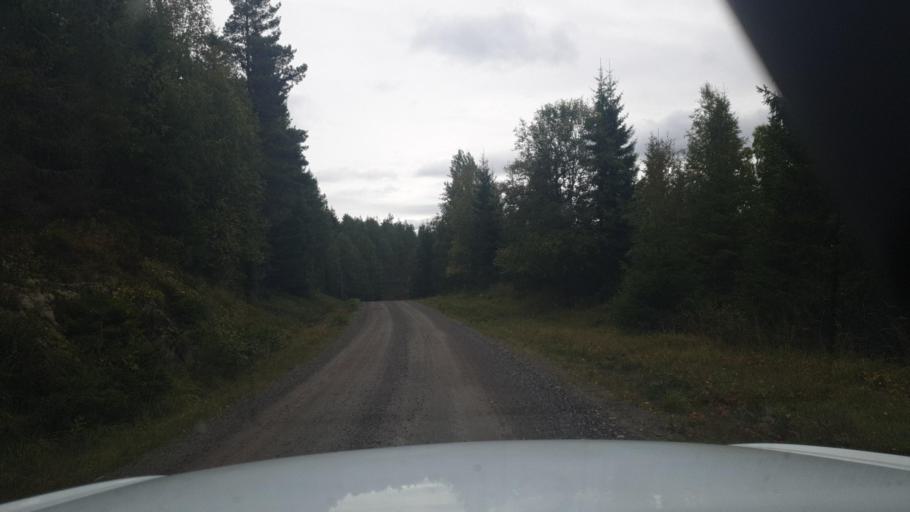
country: SE
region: Vaermland
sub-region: Eda Kommun
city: Charlottenberg
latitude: 60.1357
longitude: 12.5928
